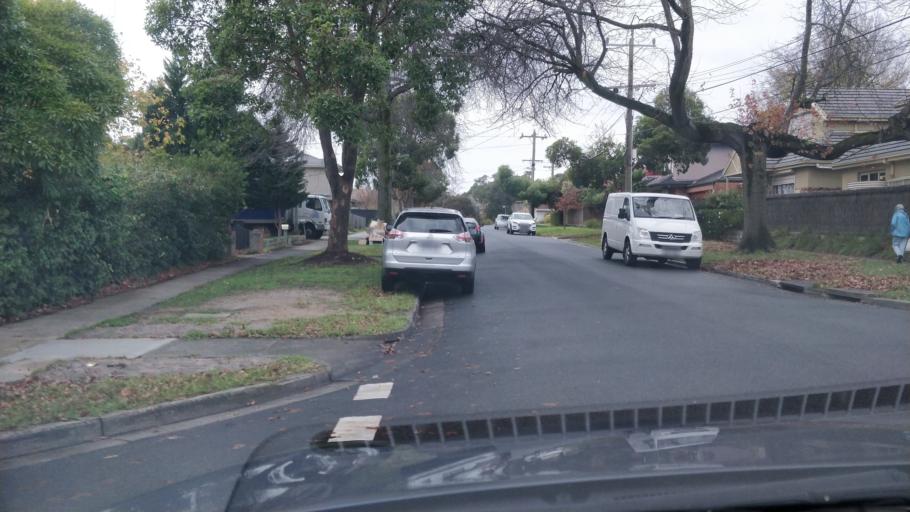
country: AU
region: Victoria
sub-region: Whitehorse
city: Nunawading
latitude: -37.8157
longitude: 145.1788
